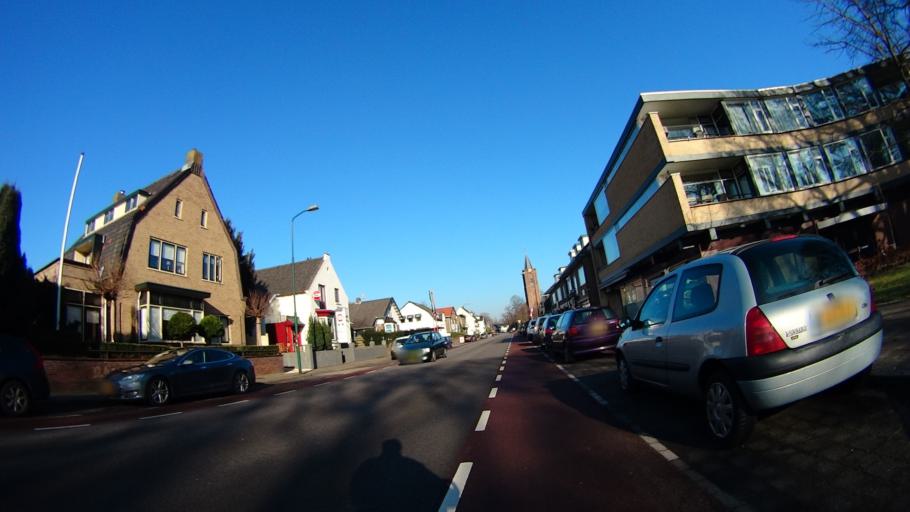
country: NL
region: Utrecht
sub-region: Gemeente Soest
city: Soest
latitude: 52.1715
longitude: 5.3112
